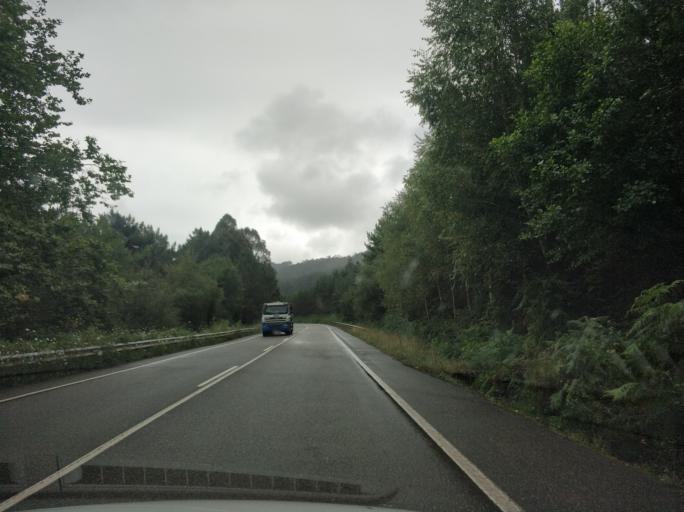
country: ES
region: Asturias
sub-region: Province of Asturias
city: Tineo
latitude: 43.5420
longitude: -6.4279
